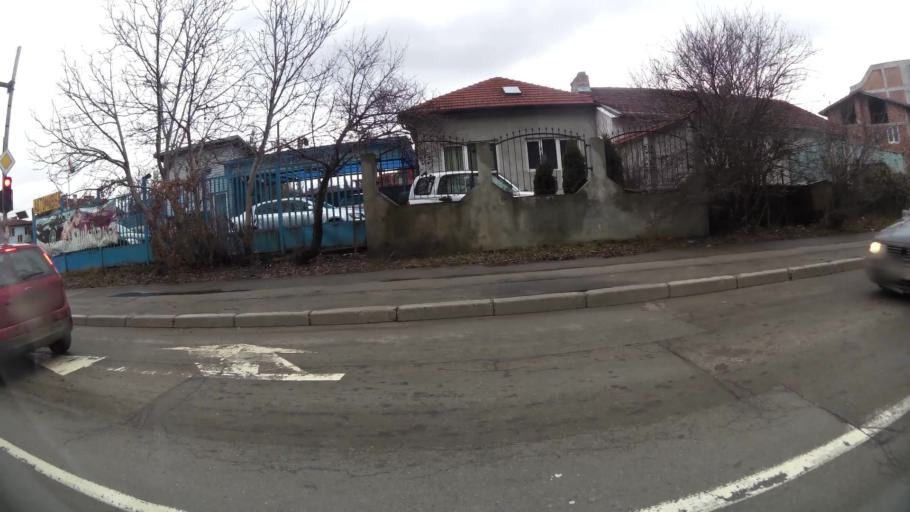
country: BG
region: Sofia-Capital
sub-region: Stolichna Obshtina
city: Sofia
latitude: 42.7269
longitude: 23.2892
